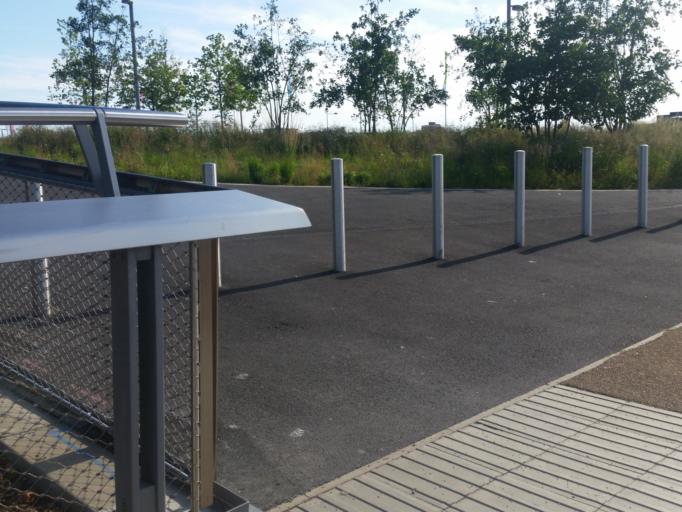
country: GB
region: England
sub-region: Greater London
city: Poplar
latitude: 51.5441
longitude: -0.0171
